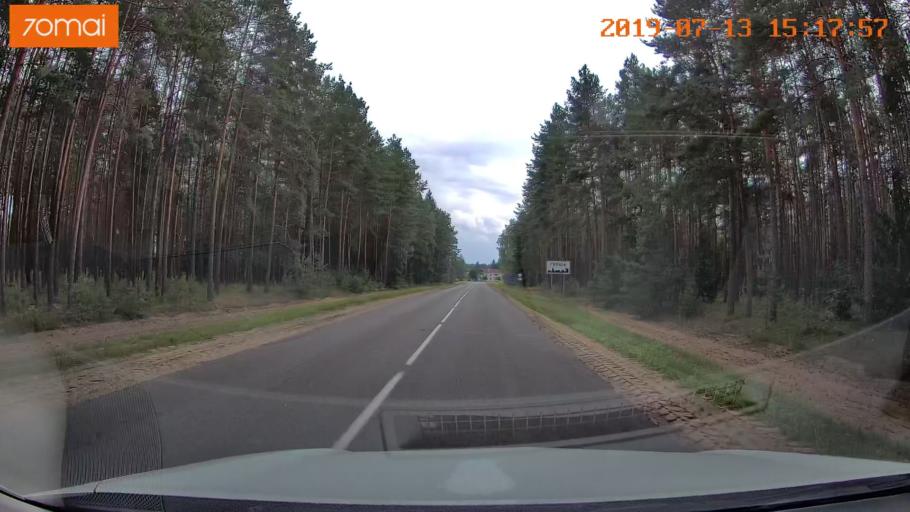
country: BY
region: Mogilev
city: Hlusha
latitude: 53.0896
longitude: 28.8460
